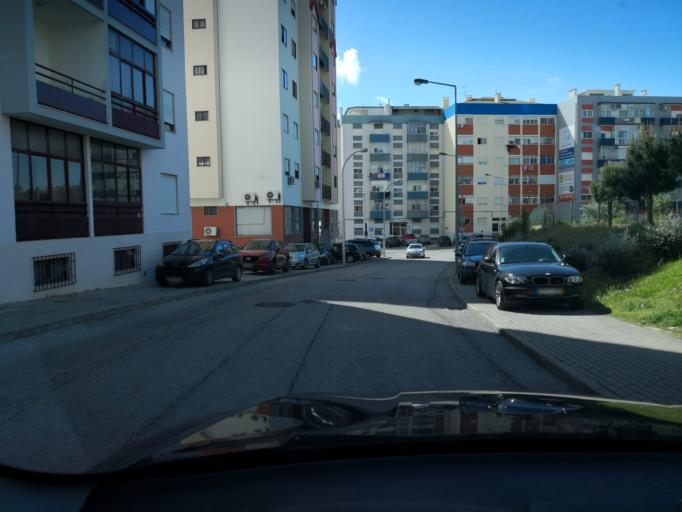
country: PT
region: Setubal
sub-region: Setubal
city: Setubal
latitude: 38.5343
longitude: -8.8702
